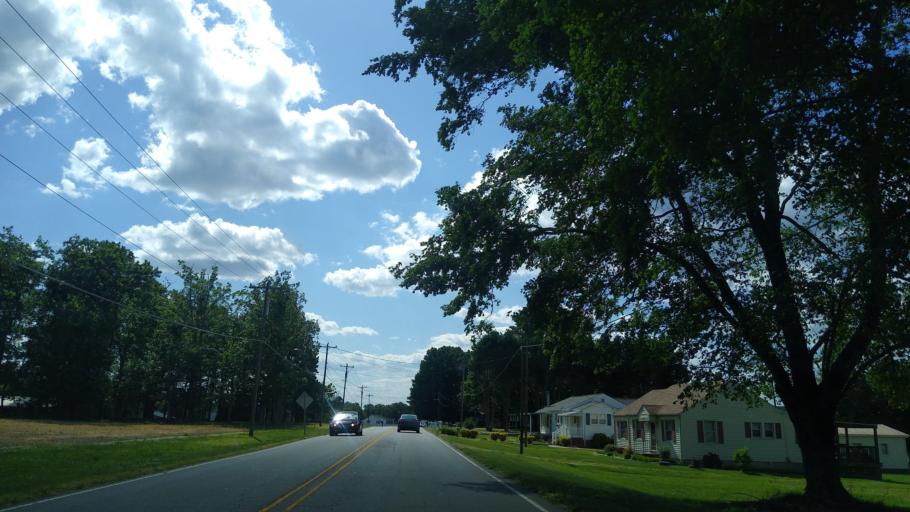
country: US
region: North Carolina
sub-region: Forsyth County
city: Kernersville
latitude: 36.1005
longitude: -80.0836
